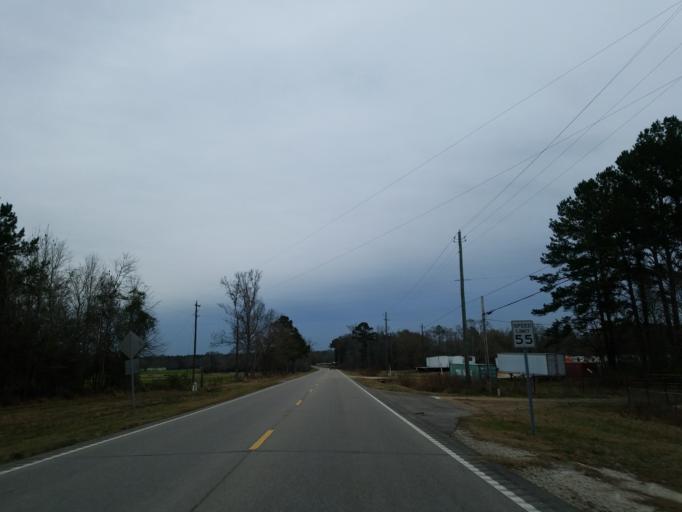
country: US
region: Mississippi
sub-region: Forrest County
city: Glendale
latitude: 31.4844
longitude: -89.2814
